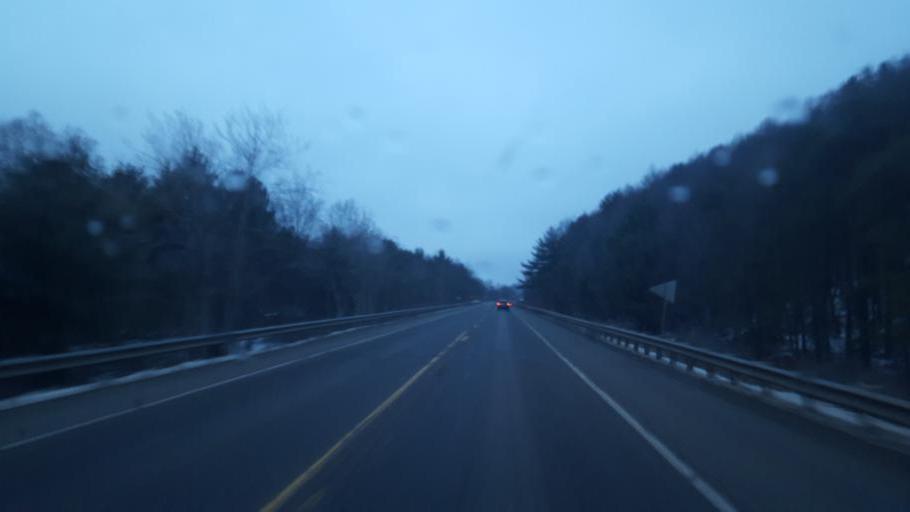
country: US
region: Pennsylvania
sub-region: McKean County
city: Port Allegany
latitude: 41.7823
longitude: -78.1531
